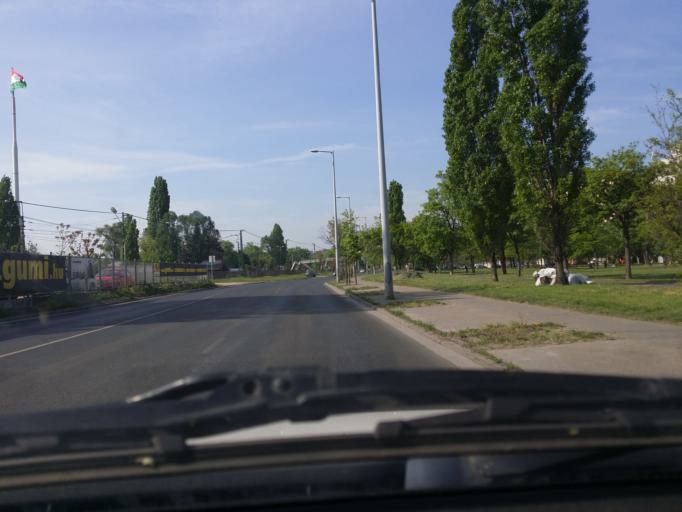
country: HU
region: Budapest
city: Budapest III. keruelet
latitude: 47.5356
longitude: 19.0458
